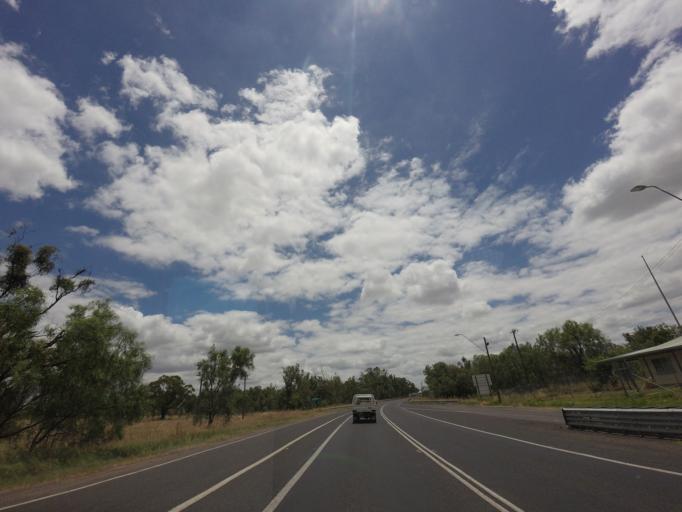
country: AU
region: Queensland
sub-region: Goondiwindi
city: Goondiwindi
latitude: -28.5605
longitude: 150.3175
